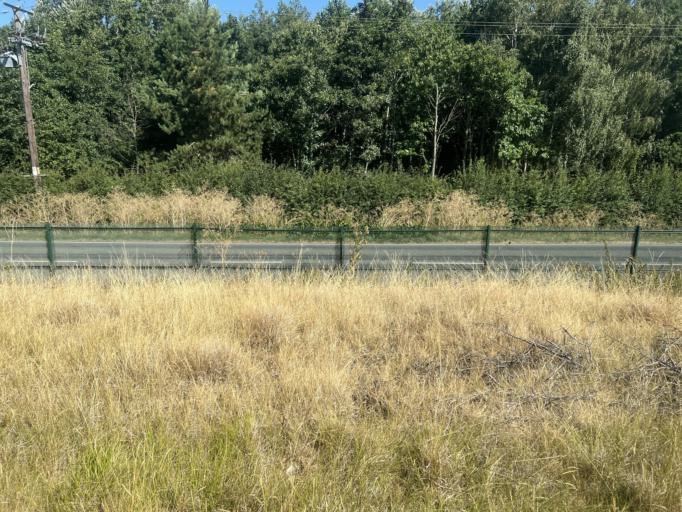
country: GB
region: England
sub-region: Lincolnshire
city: Kirton
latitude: 52.9759
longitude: -0.1172
